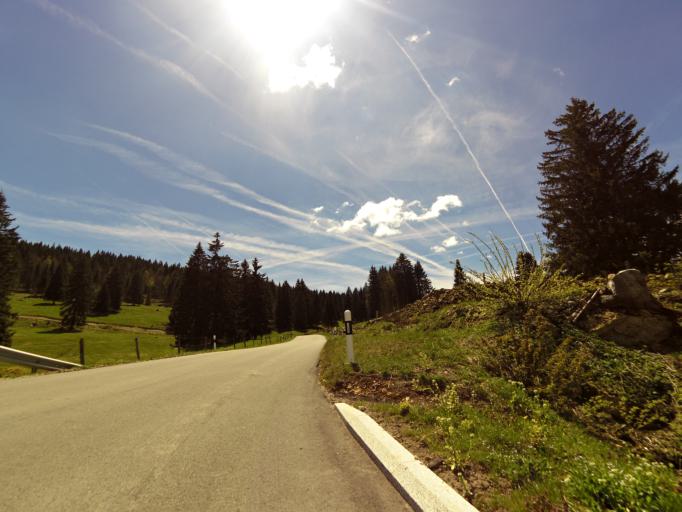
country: CH
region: Vaud
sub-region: Jura-Nord vaudois District
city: Le Chenit
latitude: 46.5744
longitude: 6.2087
